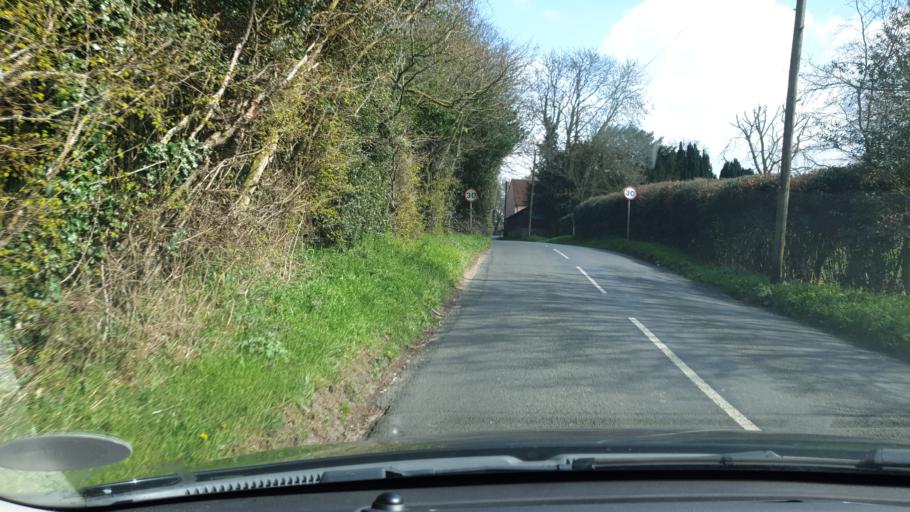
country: GB
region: England
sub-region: Essex
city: Great Bentley
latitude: 51.8746
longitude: 1.1104
